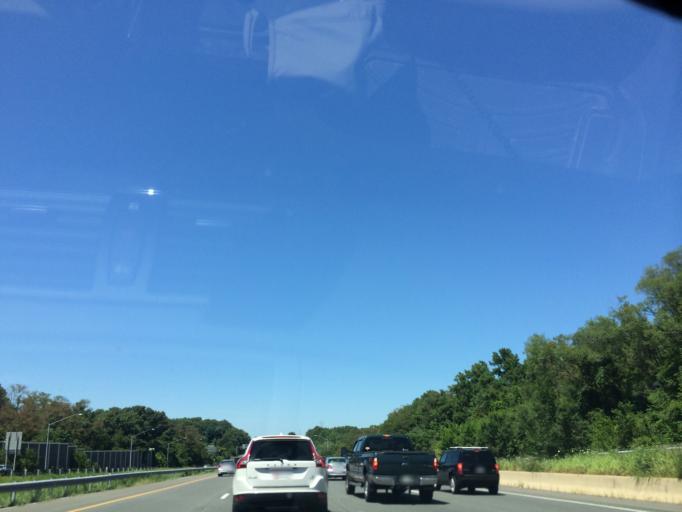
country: US
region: Maryland
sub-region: Howard County
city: Ellicott City
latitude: 39.2580
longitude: -76.8205
